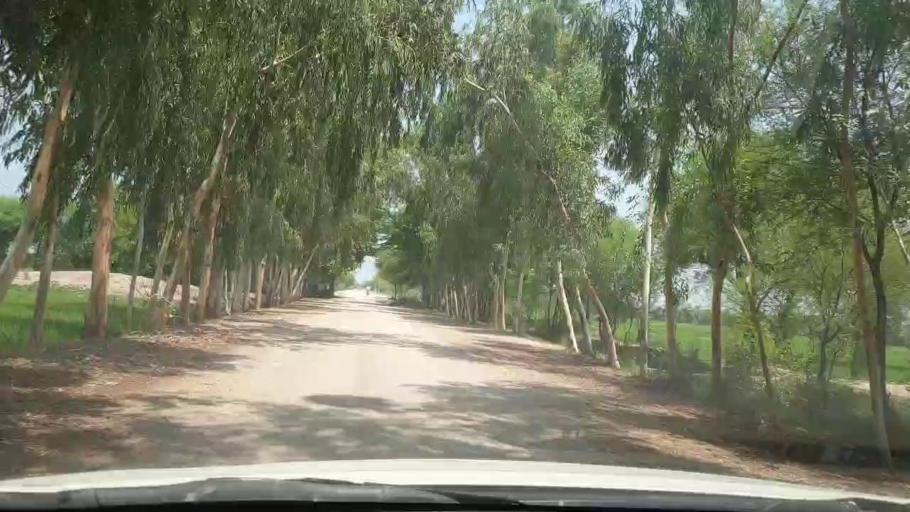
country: PK
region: Sindh
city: Rustam jo Goth
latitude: 28.0275
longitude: 68.7641
